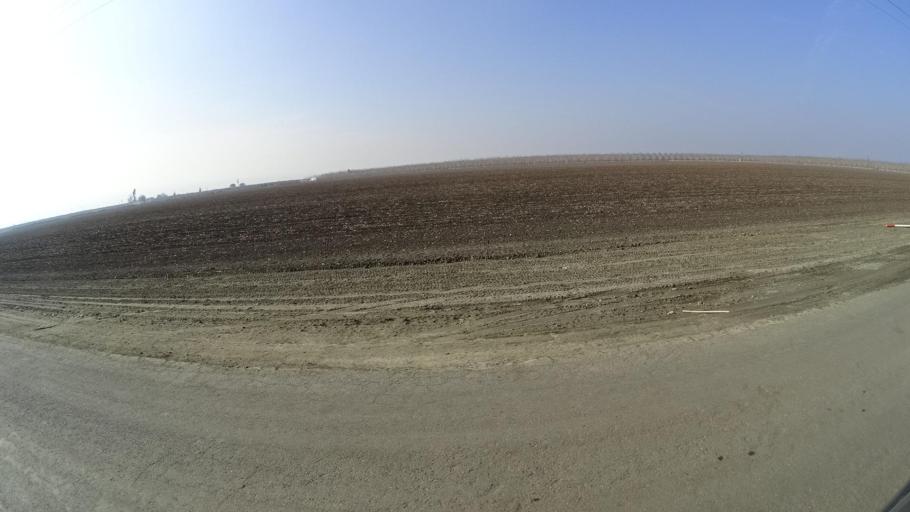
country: US
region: California
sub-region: Kern County
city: Buttonwillow
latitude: 35.3590
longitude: -119.4123
